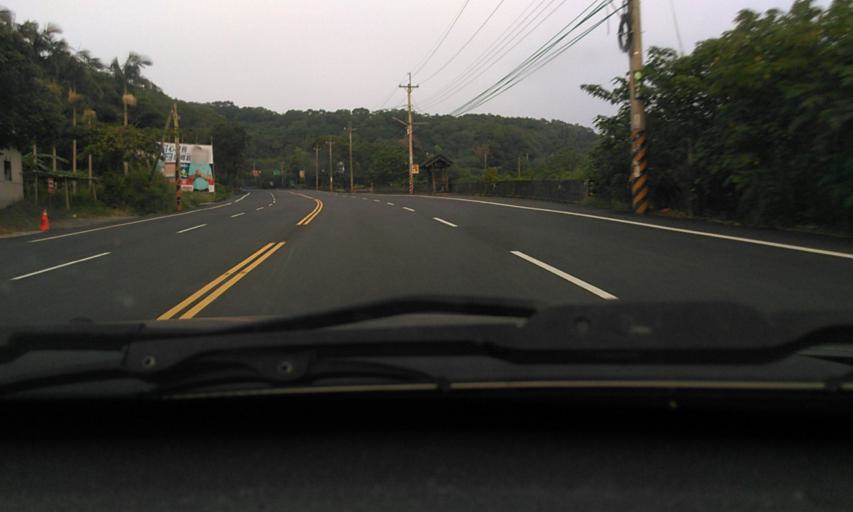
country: TW
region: Taiwan
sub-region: Hsinchu
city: Hsinchu
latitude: 24.6883
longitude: 120.9721
